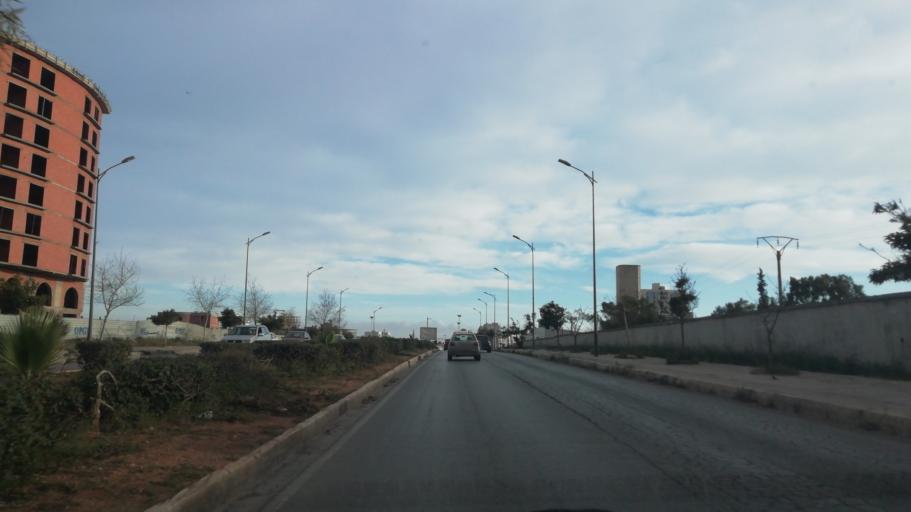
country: DZ
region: Oran
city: Bir el Djir
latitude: 35.7082
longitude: -0.5732
